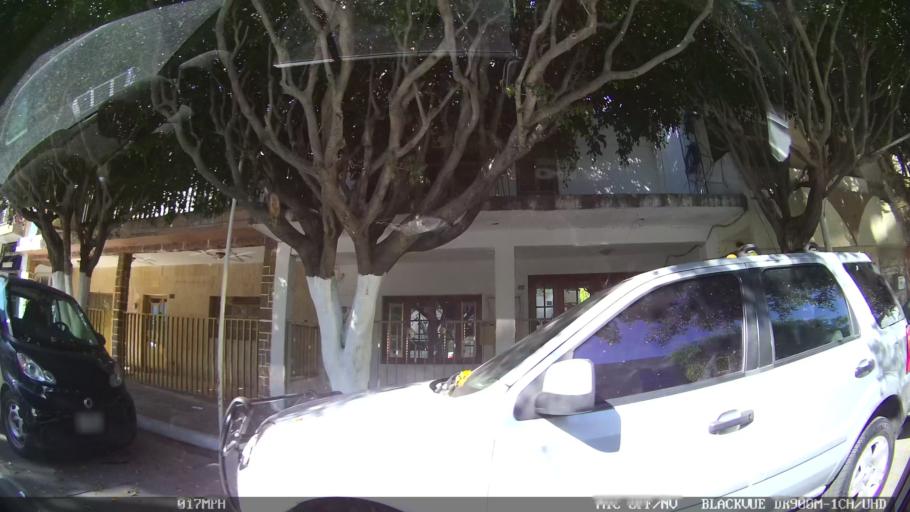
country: MX
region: Jalisco
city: Tlaquepaque
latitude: 20.6732
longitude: -103.2850
